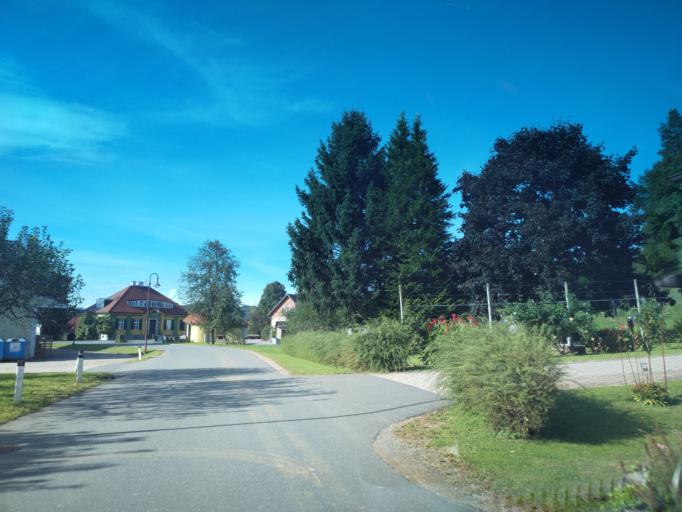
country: AT
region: Styria
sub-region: Politischer Bezirk Leibnitz
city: Sankt Johann im Saggautal
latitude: 46.6992
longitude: 15.4008
